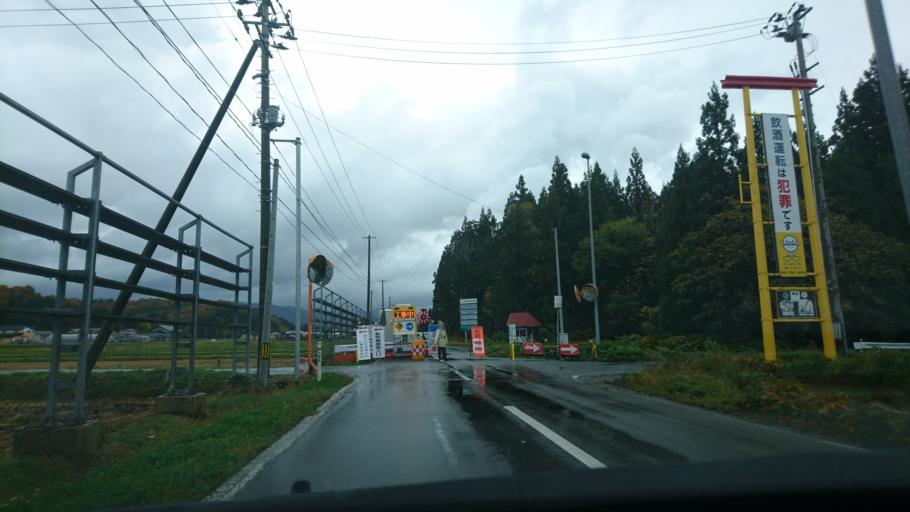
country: JP
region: Akita
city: Yokotemachi
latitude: 39.3774
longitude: 140.7600
